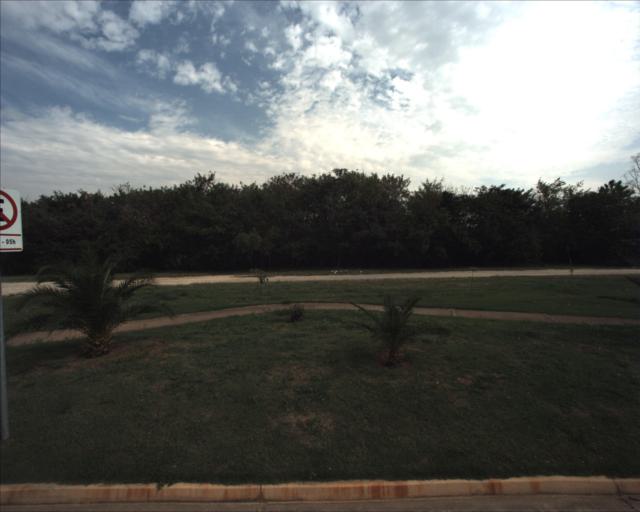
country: BR
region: Sao Paulo
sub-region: Sorocaba
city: Sorocaba
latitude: -23.4650
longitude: -47.4398
